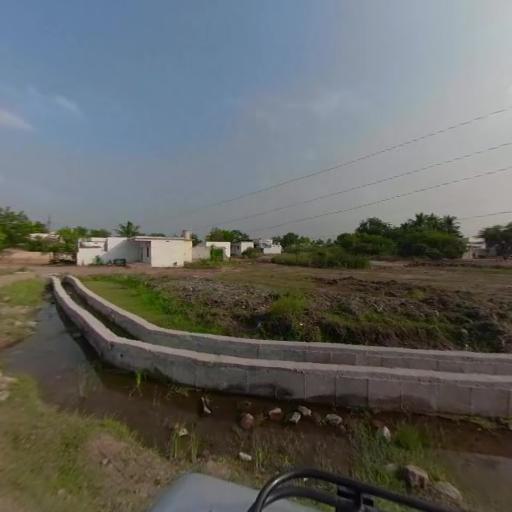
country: IN
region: Telangana
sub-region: Nalgonda
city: Suriapet
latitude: 17.1665
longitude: 79.5079
